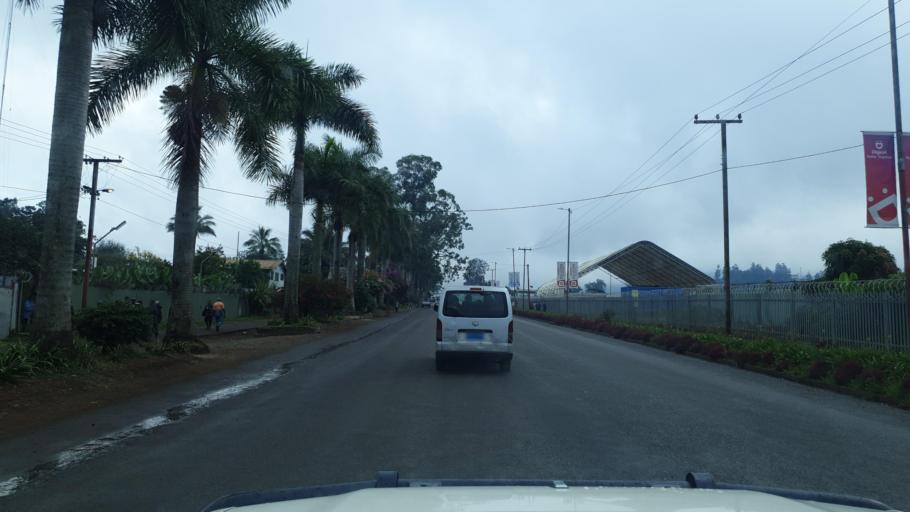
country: PG
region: Eastern Highlands
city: Goroka
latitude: -6.0805
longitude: 145.3896
